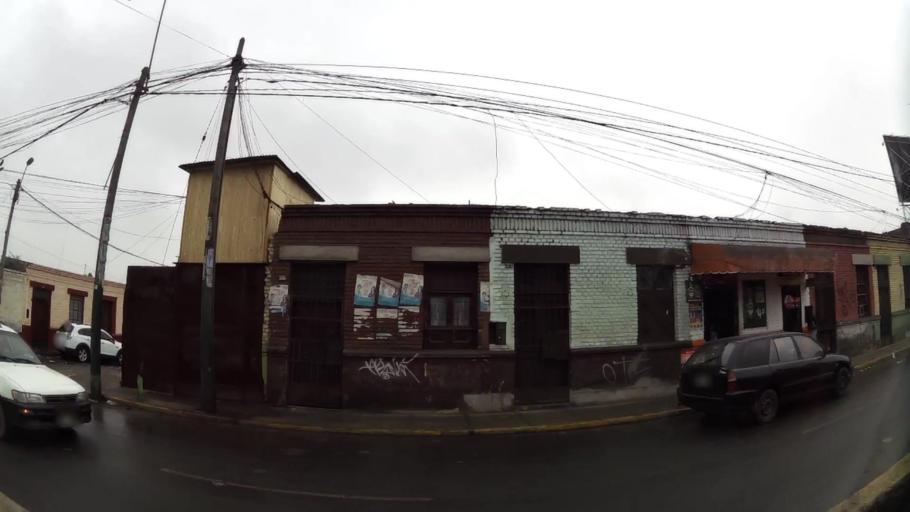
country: PE
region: Lima
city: Lima
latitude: -12.0581
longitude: -77.0172
